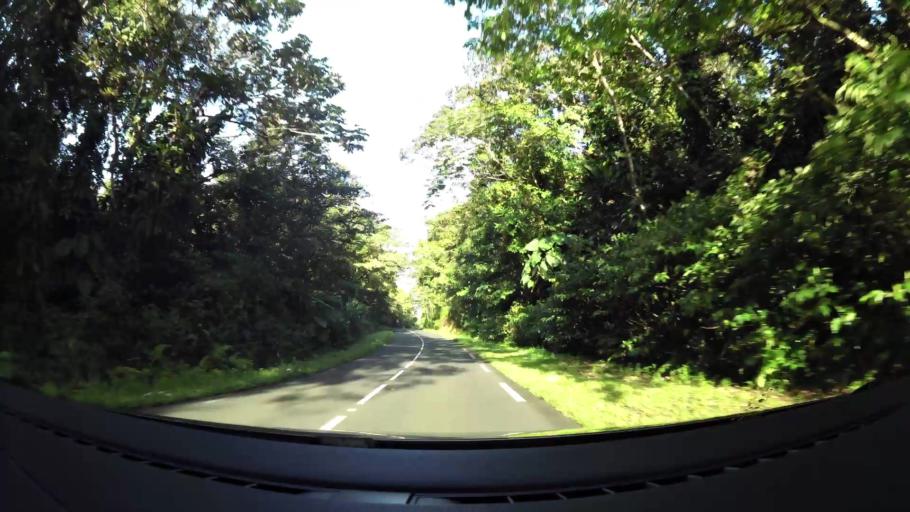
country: GP
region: Guadeloupe
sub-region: Guadeloupe
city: Bouillante
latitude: 16.1767
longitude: -61.6922
